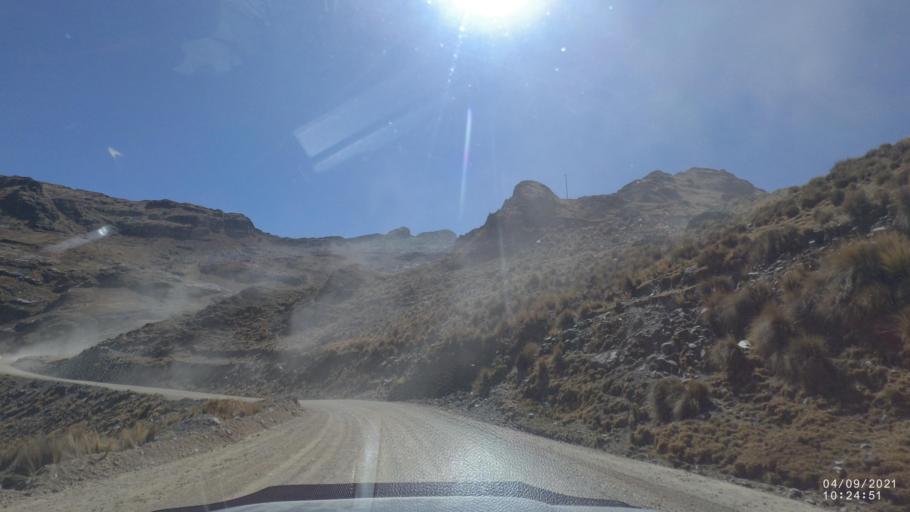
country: BO
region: Cochabamba
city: Sipe Sipe
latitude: -17.3074
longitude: -66.4371
